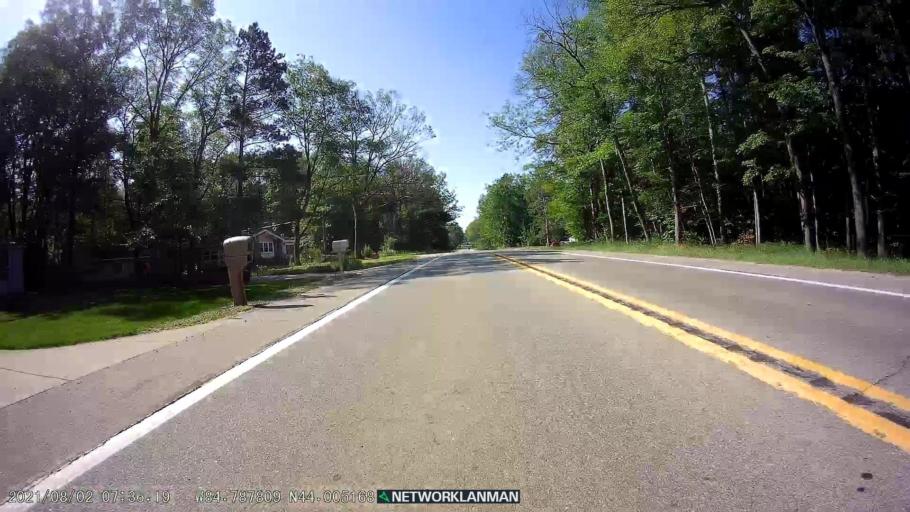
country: US
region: Michigan
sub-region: Clare County
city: Harrison
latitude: 44.0055
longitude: -84.7878
